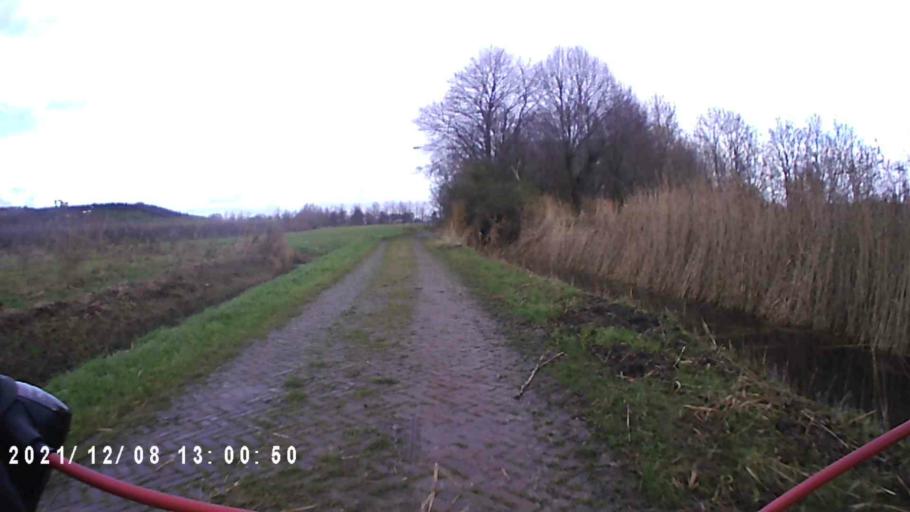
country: NL
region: Groningen
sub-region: Gemeente Haren
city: Haren
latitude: 53.2016
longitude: 6.6261
